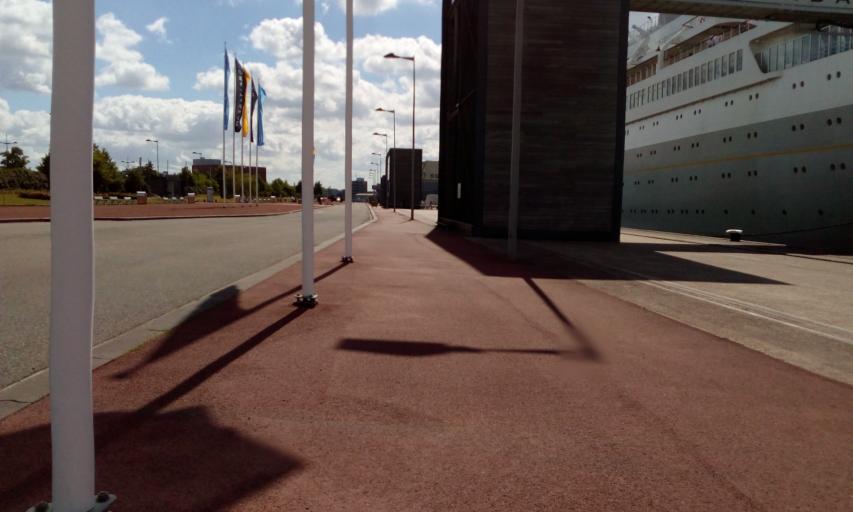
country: NL
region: South Holland
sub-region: Gemeente Rotterdam
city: Delfshaven
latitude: 51.8985
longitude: 4.4719
